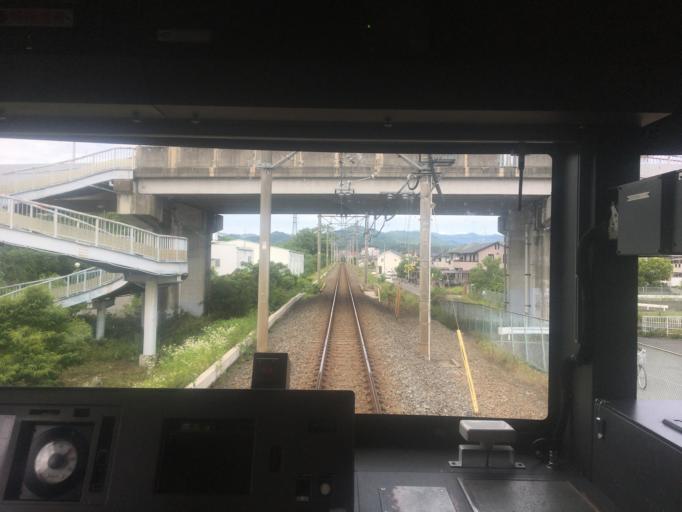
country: JP
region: Saitama
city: Ogawa
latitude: 36.0569
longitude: 139.2723
